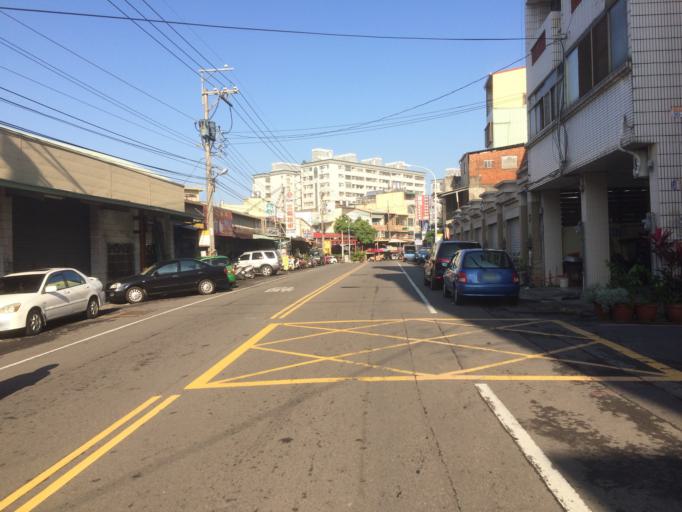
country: TW
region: Taiwan
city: Fengyuan
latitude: 24.2073
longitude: 120.7109
